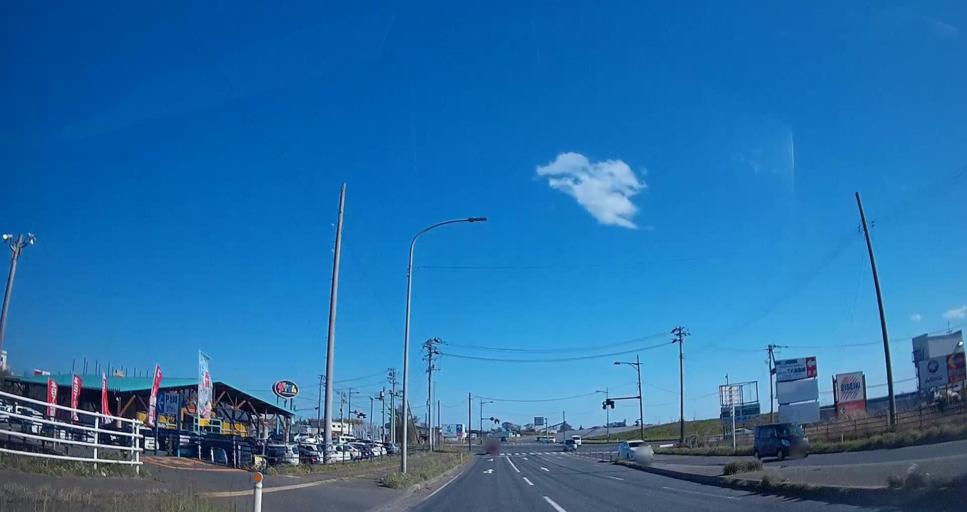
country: JP
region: Miyagi
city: Yamoto
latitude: 38.4323
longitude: 141.2484
